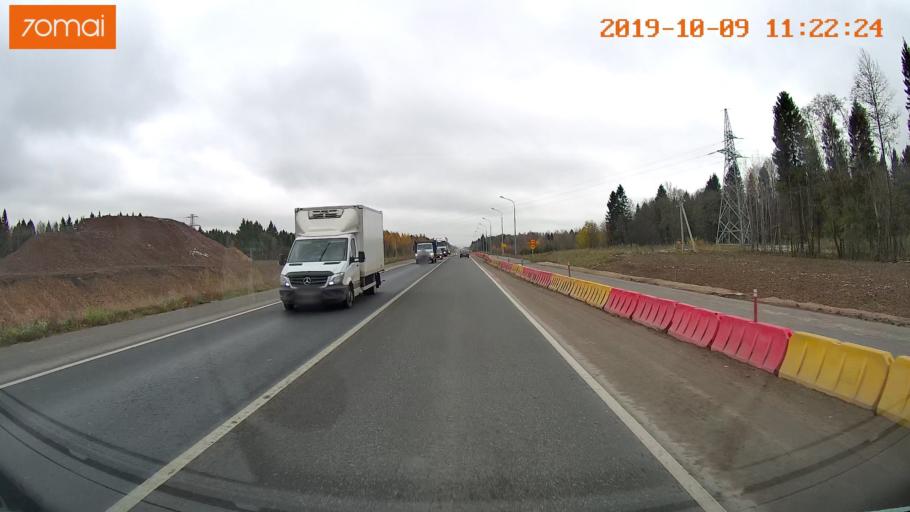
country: RU
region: Vologda
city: Vologda
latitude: 59.1319
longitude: 39.9577
